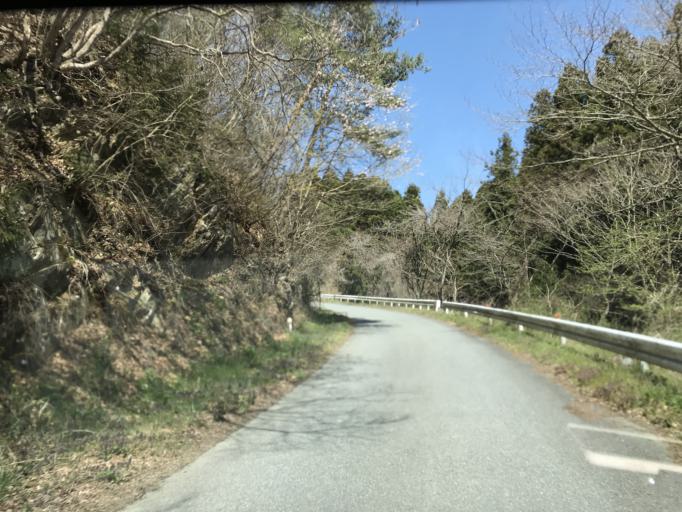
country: JP
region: Iwate
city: Ichinoseki
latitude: 38.8218
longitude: 141.2836
